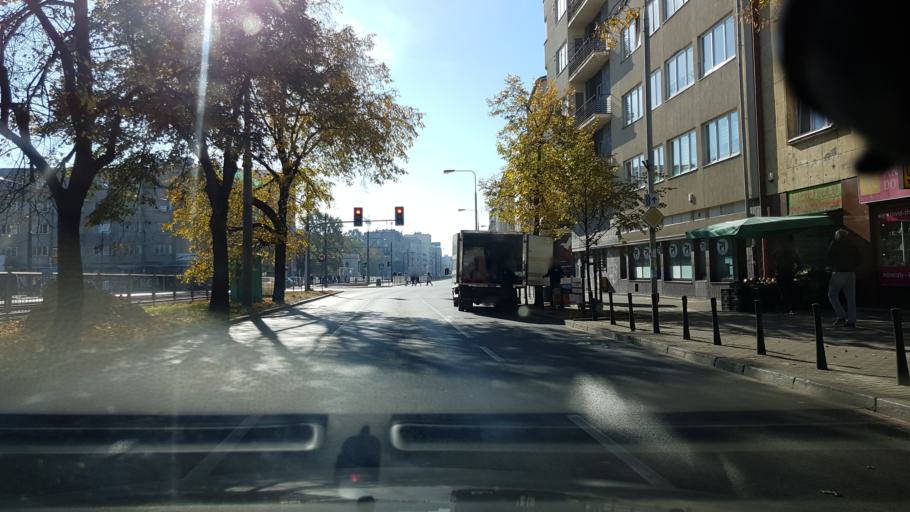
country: PL
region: Masovian Voivodeship
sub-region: Warszawa
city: Mokotow
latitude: 52.2061
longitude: 21.0224
